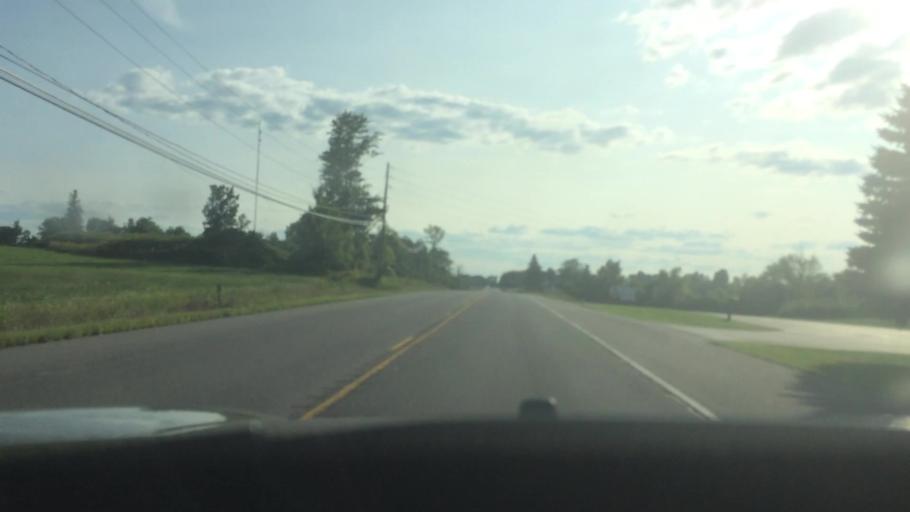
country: US
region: New York
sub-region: St. Lawrence County
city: Potsdam
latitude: 44.6465
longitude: -75.0549
